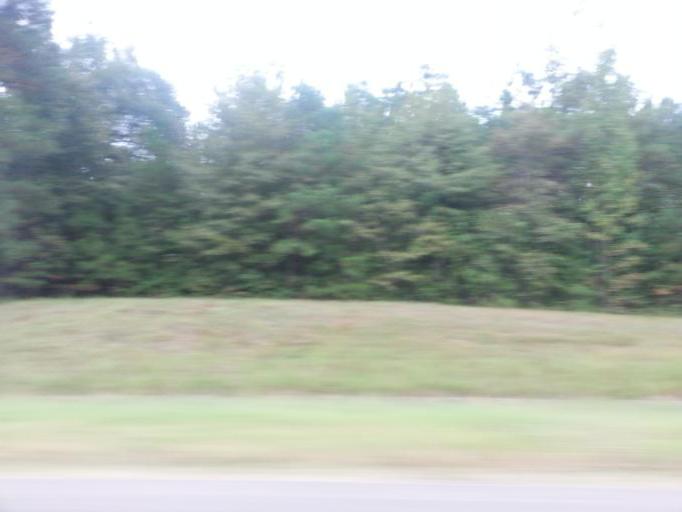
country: US
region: Alabama
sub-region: Butler County
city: Georgiana
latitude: 31.6191
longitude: -86.8072
